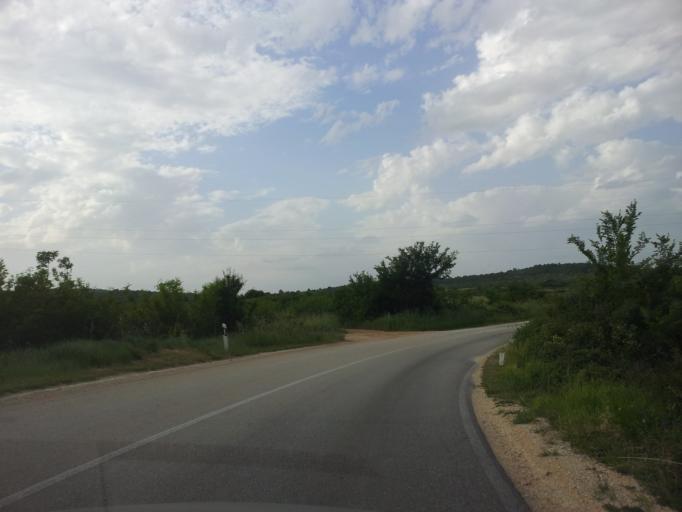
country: HR
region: Zadarska
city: Sukosan
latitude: 44.0563
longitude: 15.3333
